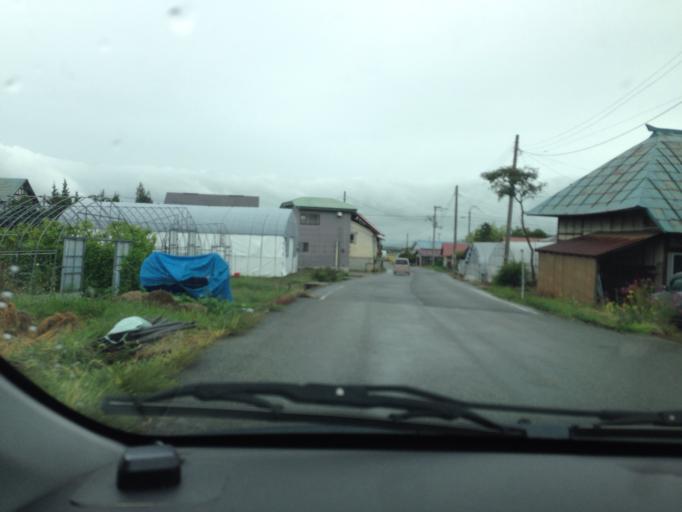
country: JP
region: Fukushima
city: Kitakata
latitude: 37.5237
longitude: 139.8189
